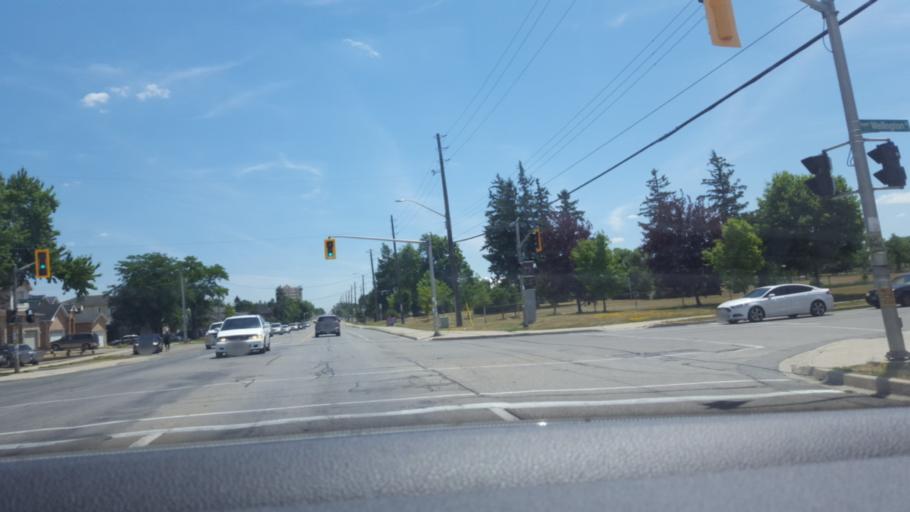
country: CA
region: Ontario
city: Hamilton
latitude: 43.2001
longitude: -79.8837
